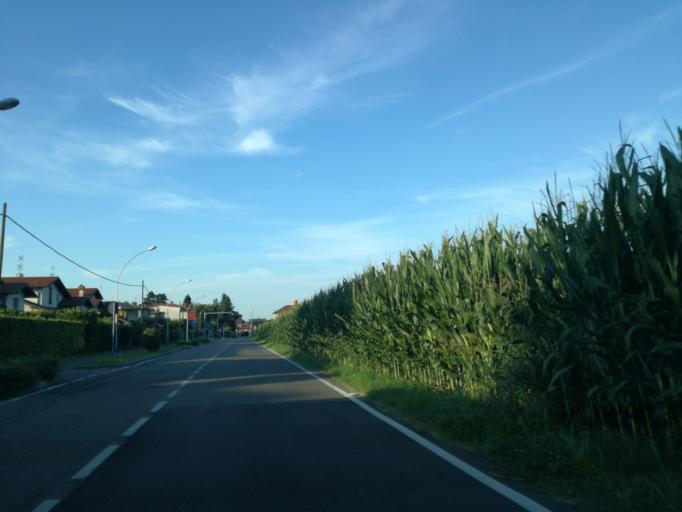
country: IT
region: Lombardy
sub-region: Provincia di Monza e Brianza
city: Sulbiate
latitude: 45.6446
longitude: 9.4285
